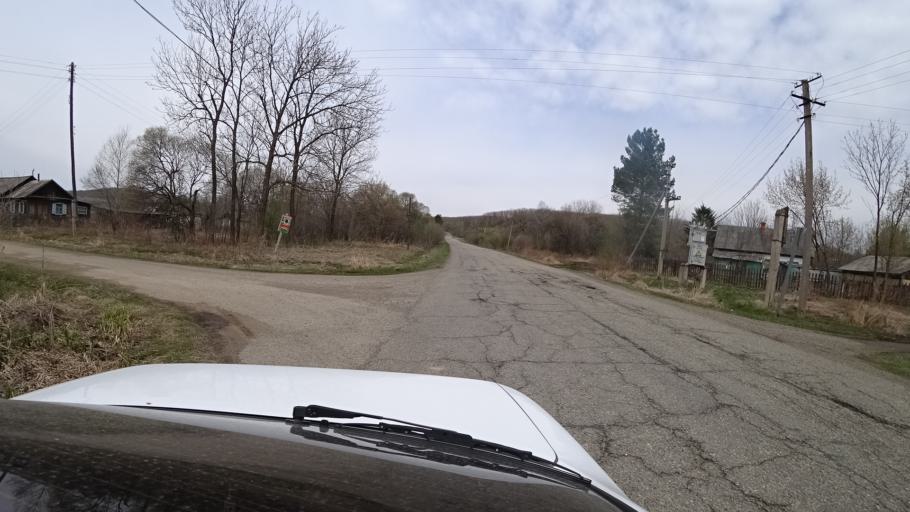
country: RU
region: Primorskiy
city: Novopokrovka
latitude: 45.7883
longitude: 134.1142
